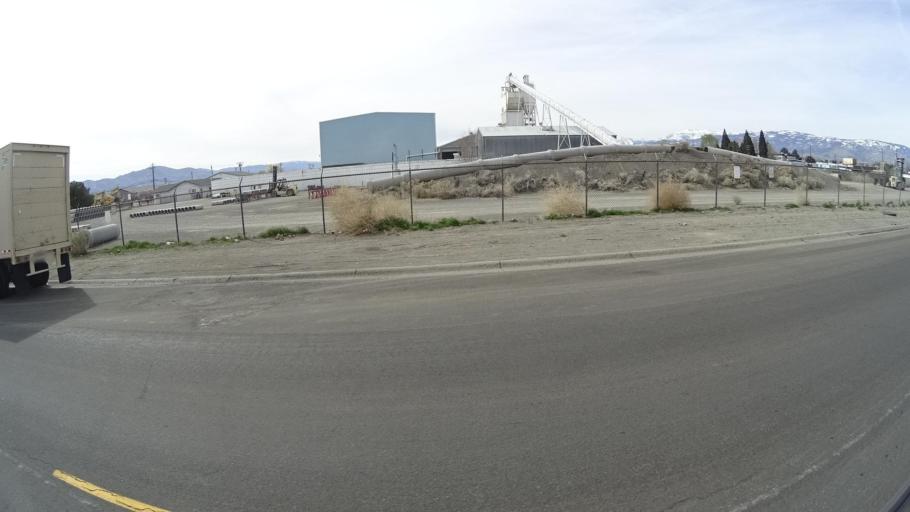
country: US
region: Nevada
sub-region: Washoe County
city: Sparks
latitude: 39.5255
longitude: -119.7550
